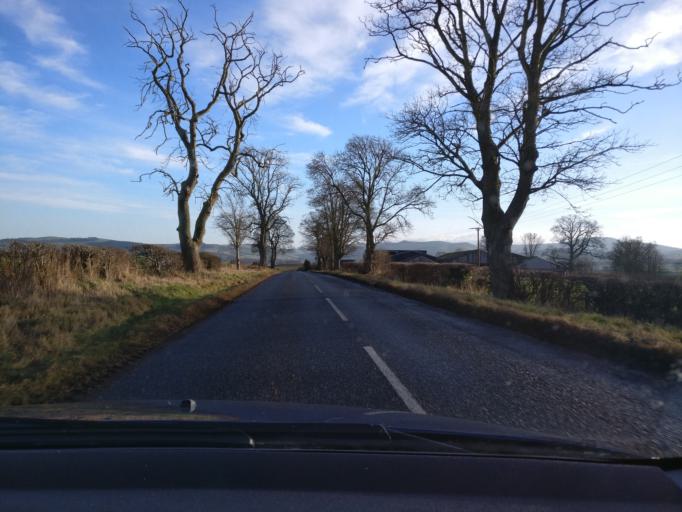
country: GB
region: Scotland
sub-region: The Scottish Borders
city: Kelso
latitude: 55.5271
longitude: -2.4215
